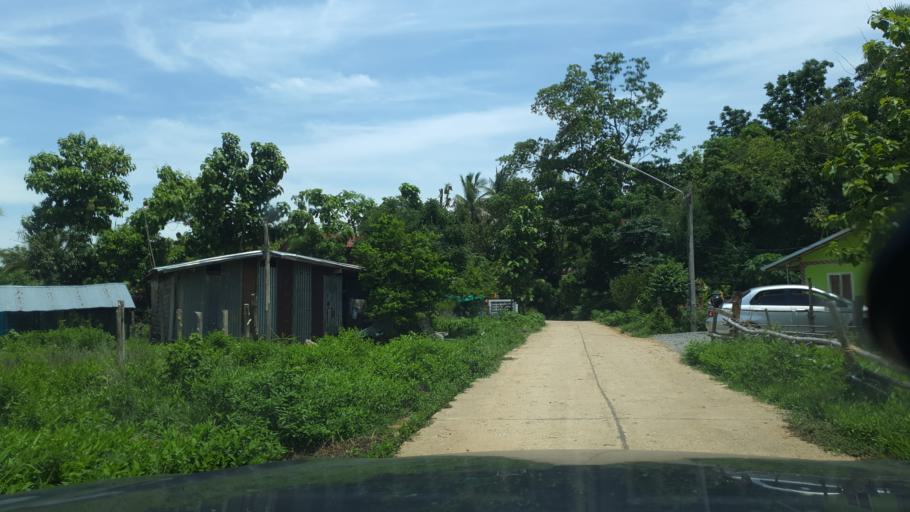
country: TH
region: Sukhothai
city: Ban Na
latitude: 17.0861
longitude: 99.6881
